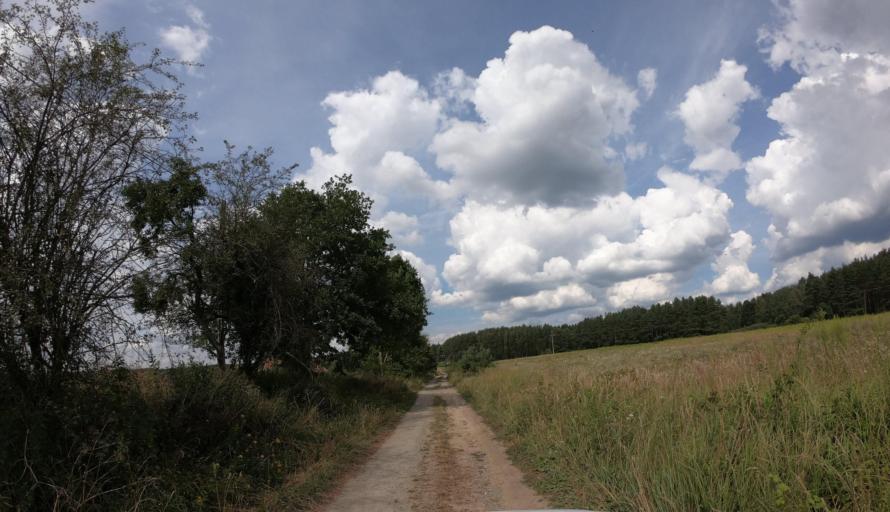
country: PL
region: West Pomeranian Voivodeship
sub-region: Powiat stargardzki
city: Kobylanka
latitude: 53.3251
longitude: 14.8226
